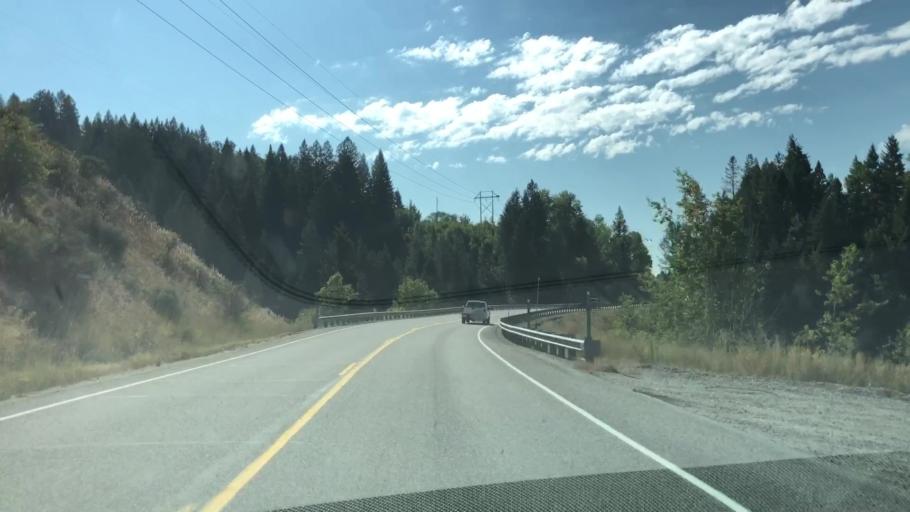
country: US
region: Idaho
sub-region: Teton County
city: Victor
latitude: 43.3003
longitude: -111.1302
